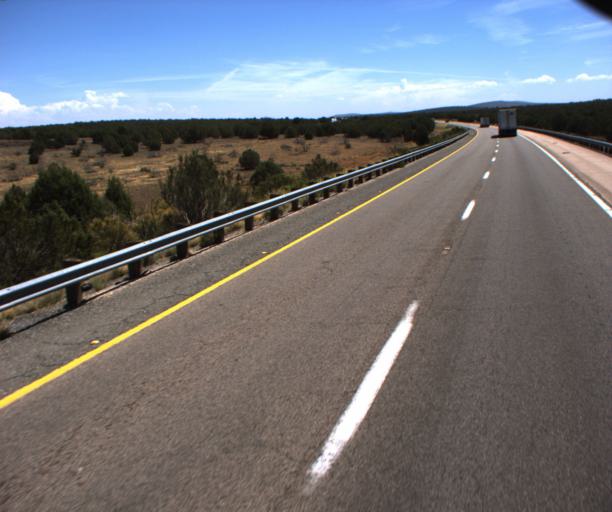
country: US
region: Arizona
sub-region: Mohave County
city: Peach Springs
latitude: 35.2072
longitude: -113.2765
